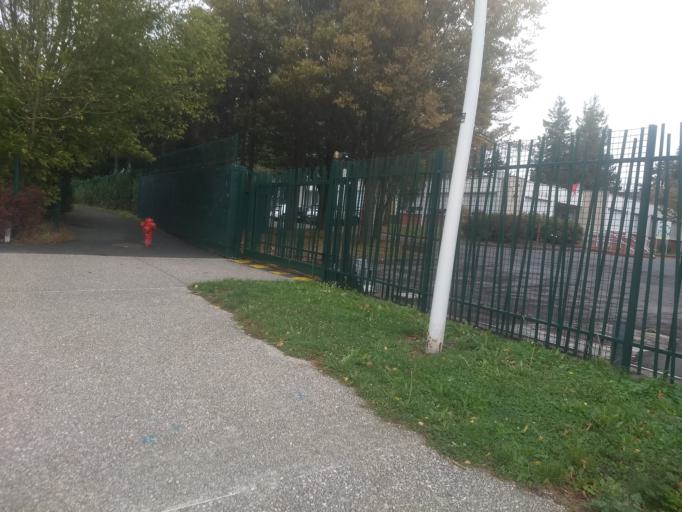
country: FR
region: Nord-Pas-de-Calais
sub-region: Departement du Pas-de-Calais
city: Saint-Nicolas
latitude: 50.3067
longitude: 2.7937
